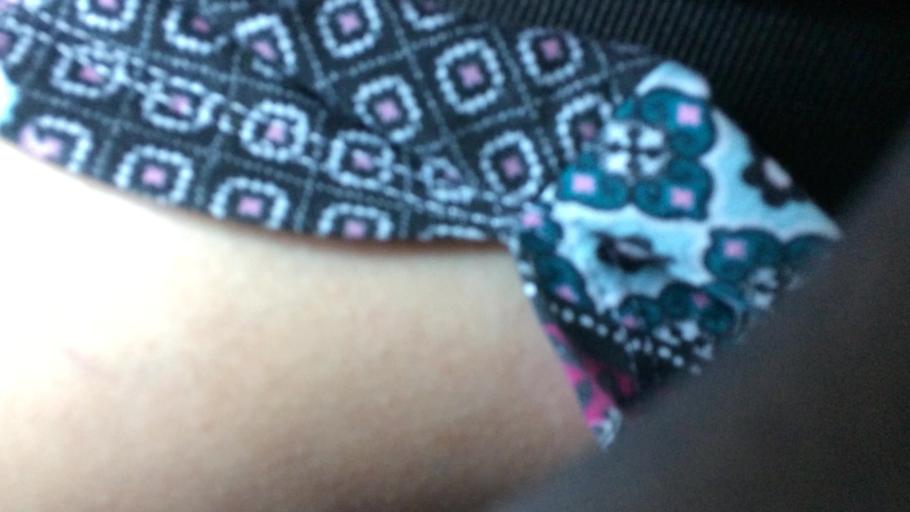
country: US
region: New Mexico
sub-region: Colfax County
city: Springer
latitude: 35.9334
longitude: -104.7947
